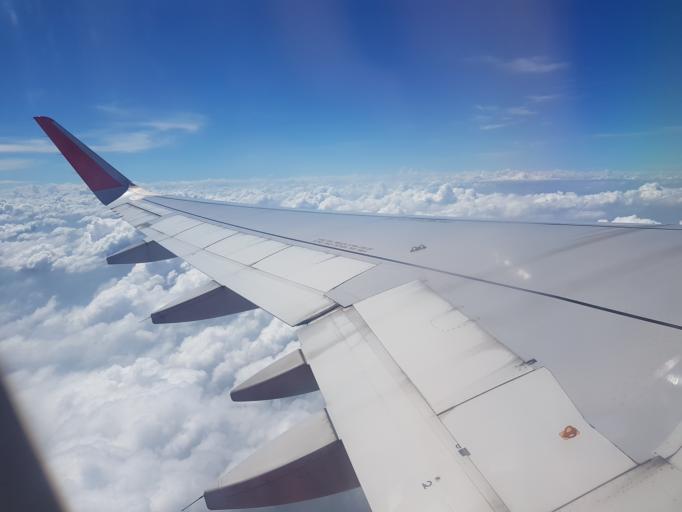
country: VN
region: Ho Chi Minh City
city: Quan Phu Nhuan
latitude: 10.8219
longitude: 106.6700
